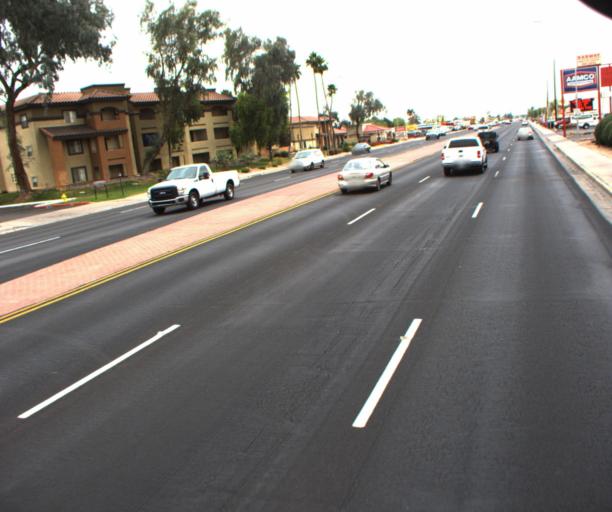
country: US
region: Arizona
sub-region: Maricopa County
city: Mesa
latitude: 33.3999
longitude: -111.8402
